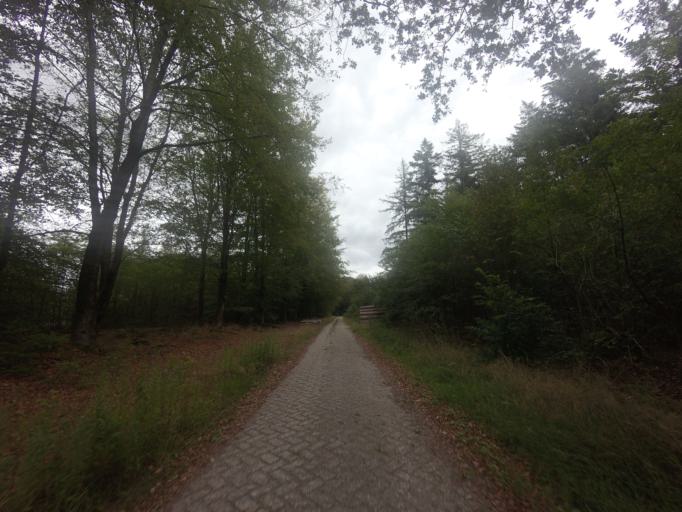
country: NL
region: Drenthe
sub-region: Gemeente Westerveld
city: Dwingeloo
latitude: 52.9227
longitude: 6.3361
